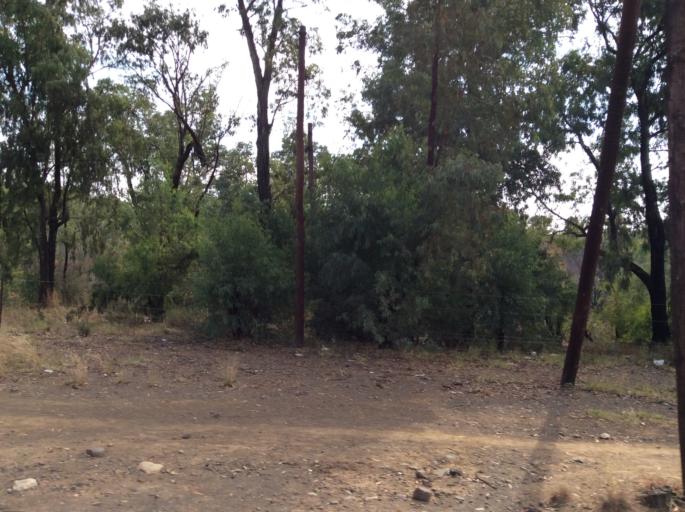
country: ZA
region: Orange Free State
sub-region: Xhariep District Municipality
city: Dewetsdorp
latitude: -29.5785
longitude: 26.6742
